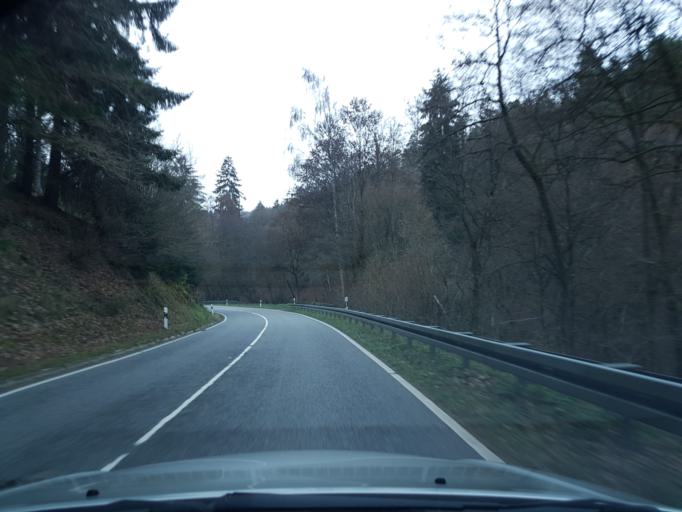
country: DE
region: Hesse
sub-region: Regierungsbezirk Darmstadt
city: Bad Schwalbach
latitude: 50.1178
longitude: 7.9820
